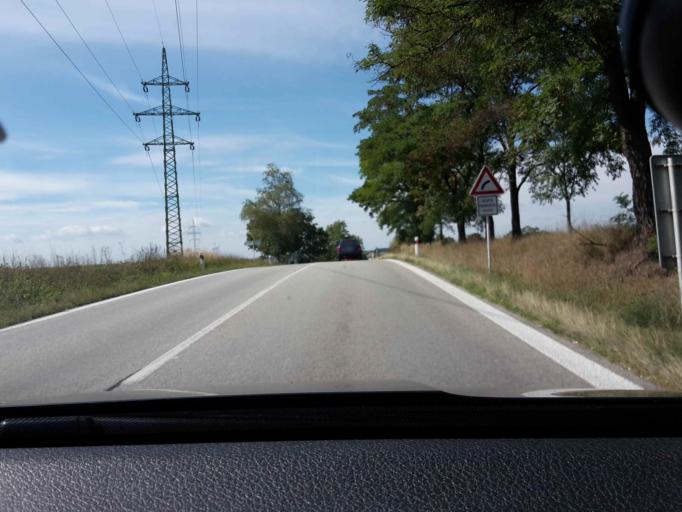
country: CZ
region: Jihocesky
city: Kardasova Recice
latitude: 49.1755
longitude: 14.8719
